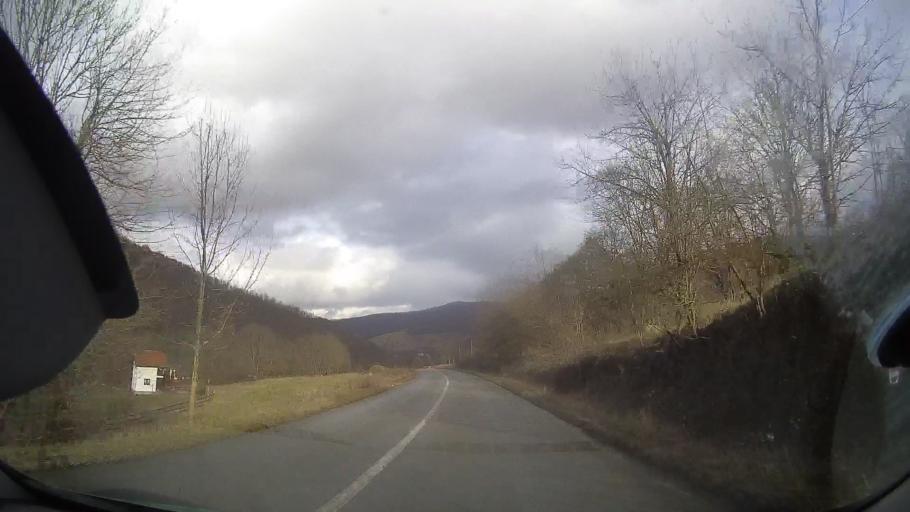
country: RO
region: Alba
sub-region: Comuna Rimetea
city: Rimetea
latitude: 46.4665
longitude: 23.5765
